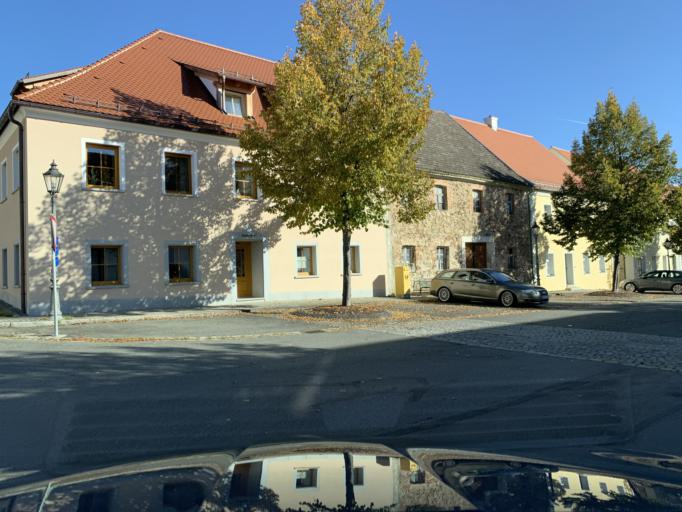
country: DE
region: Bavaria
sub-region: Upper Palatinate
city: Winklarn
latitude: 49.4261
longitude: 12.4800
